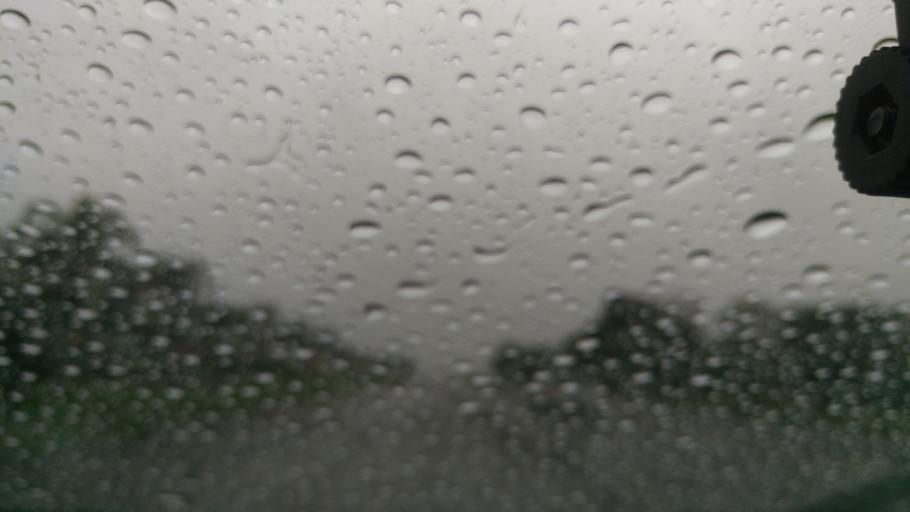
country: ZA
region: Gauteng
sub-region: West Rand District Municipality
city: Muldersdriseloop
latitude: -26.0505
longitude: 27.9503
